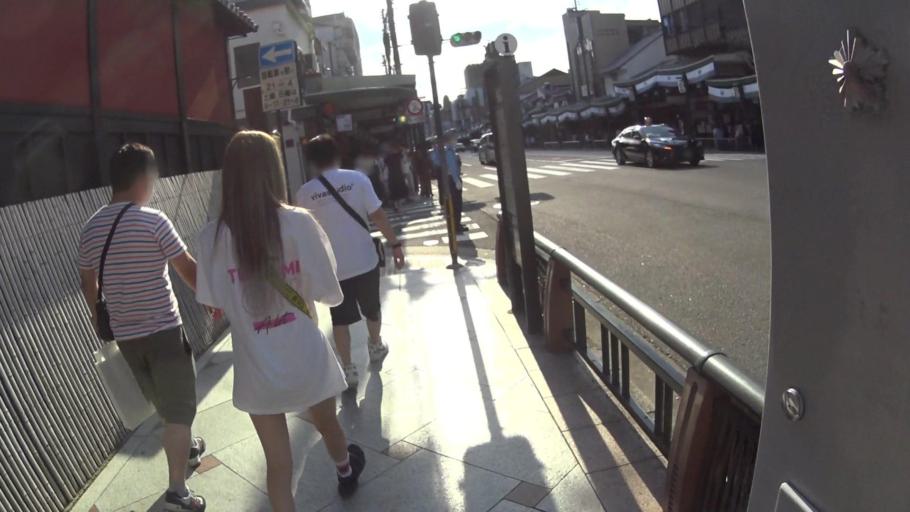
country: RU
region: Rostov
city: Remontnoye
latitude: 46.5028
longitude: 43.7472
